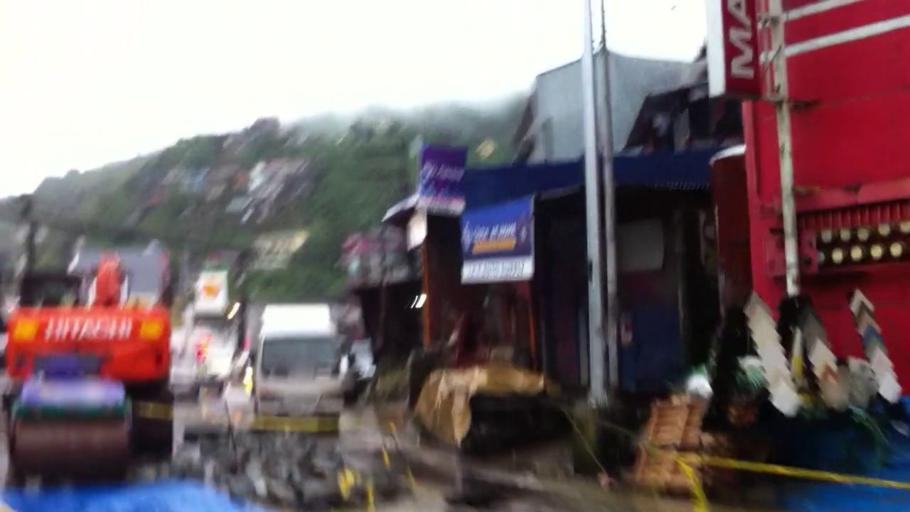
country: PH
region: Cordillera
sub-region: Province of Benguet
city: La Trinidad
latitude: 16.4402
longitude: 120.5946
